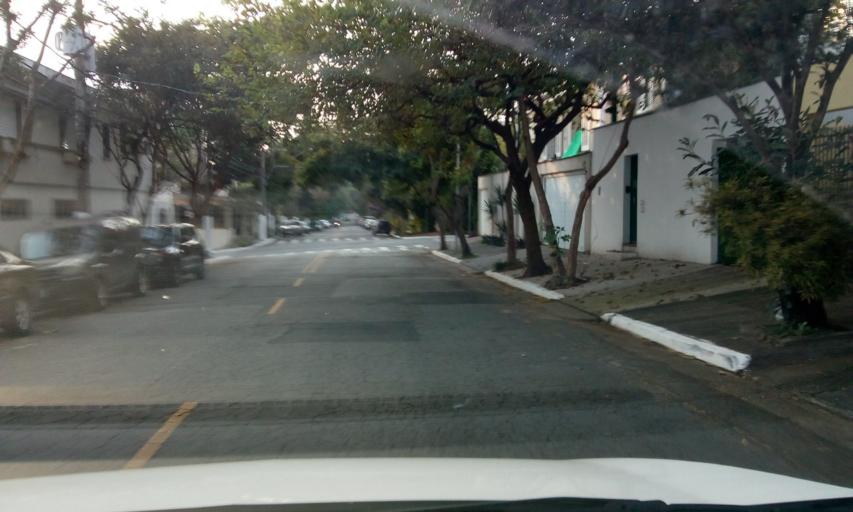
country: BR
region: Sao Paulo
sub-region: Sao Paulo
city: Sao Paulo
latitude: -23.6155
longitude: -46.6508
